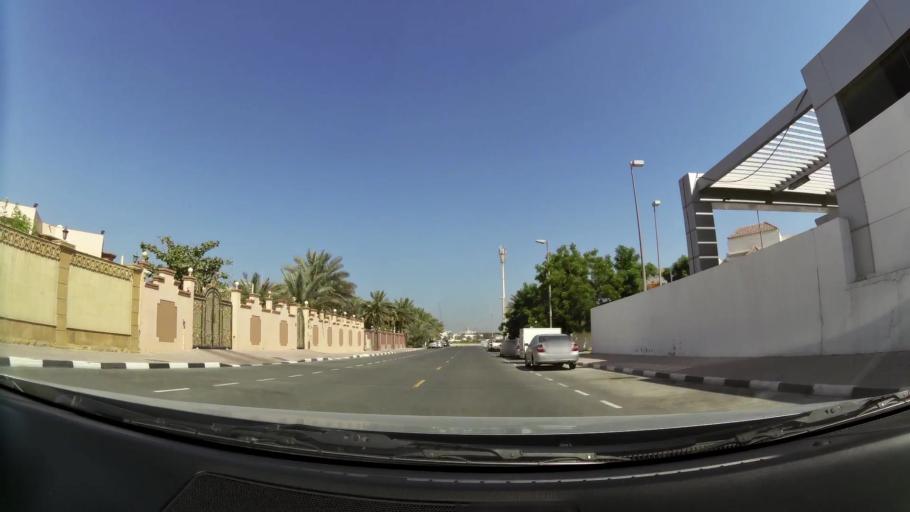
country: AE
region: Ash Shariqah
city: Sharjah
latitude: 25.2477
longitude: 55.2821
